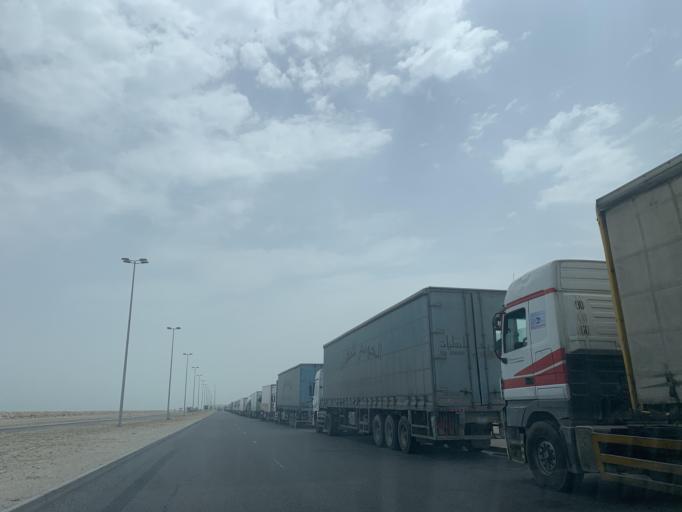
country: BH
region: Muharraq
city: Al Hadd
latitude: 26.2039
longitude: 50.7079
